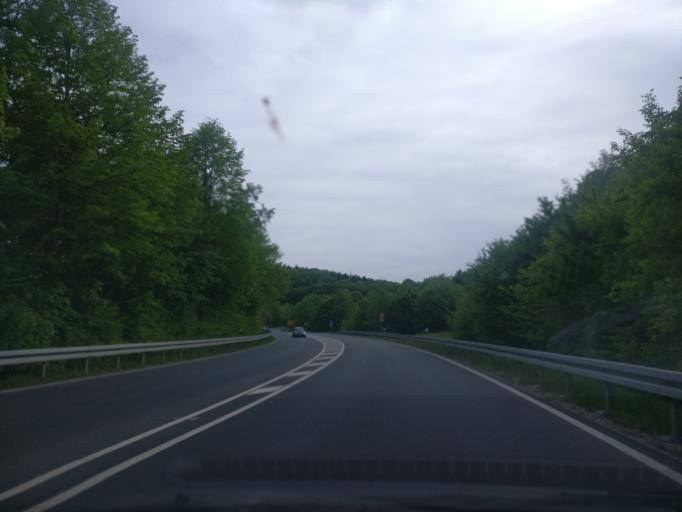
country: DE
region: Hesse
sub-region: Regierungsbezirk Kassel
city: Fuldatal
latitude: 51.3681
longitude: 9.5305
